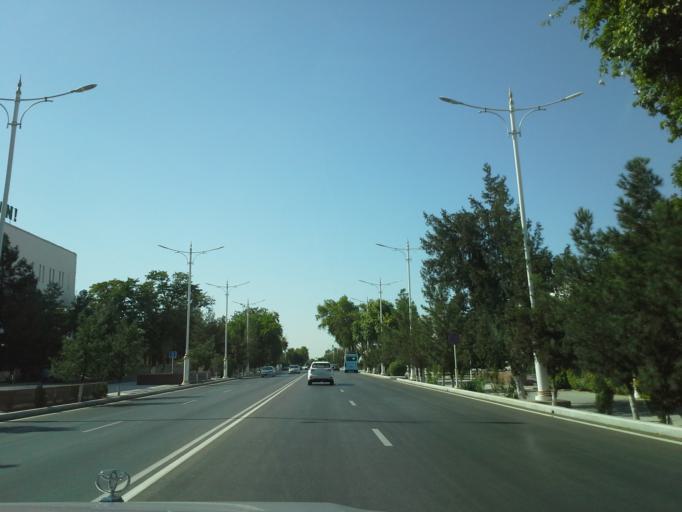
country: TM
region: Ahal
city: Ashgabat
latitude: 37.9410
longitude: 58.3902
